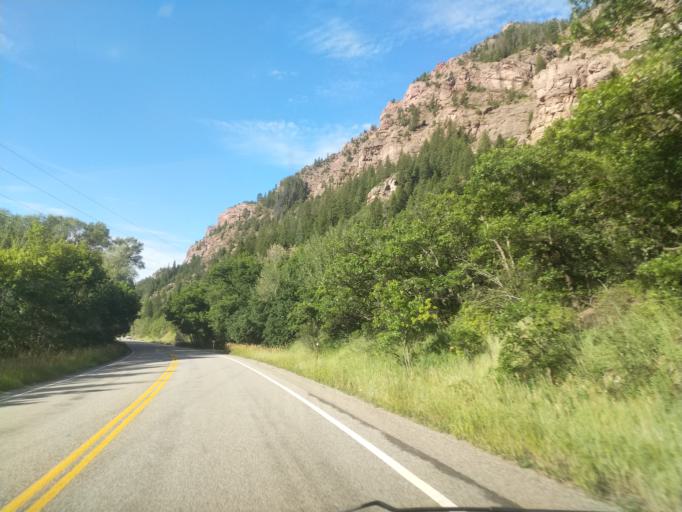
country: US
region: Colorado
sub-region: Garfield County
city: Carbondale
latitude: 39.2118
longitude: -107.2304
